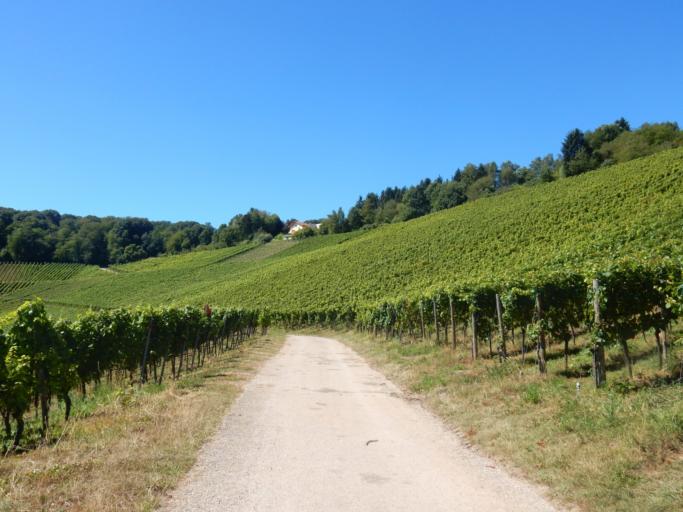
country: LU
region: Grevenmacher
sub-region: Canton de Remich
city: Bous
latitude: 49.5312
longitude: 6.3411
